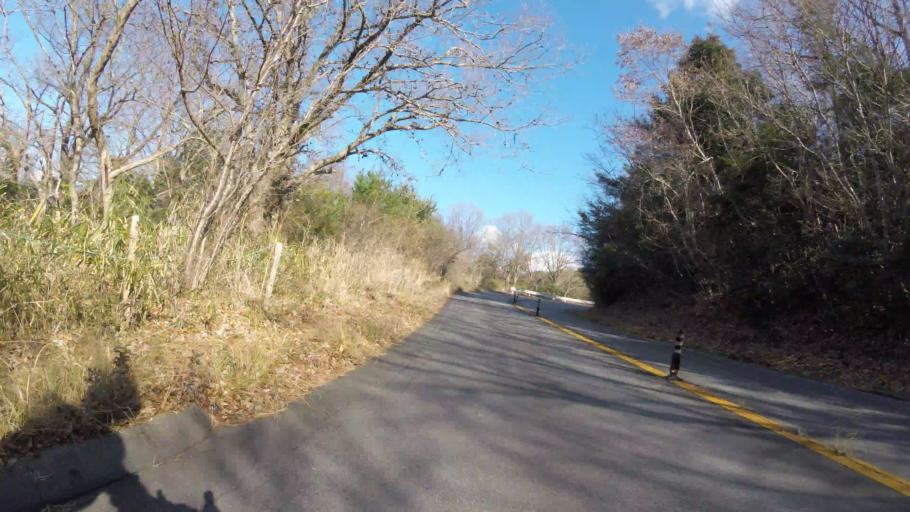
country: JP
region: Shizuoka
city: Mishima
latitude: 35.0616
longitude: 138.9806
